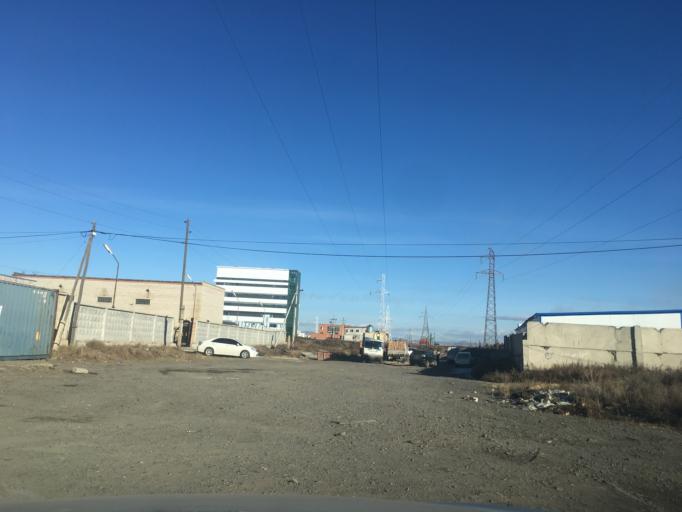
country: MN
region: Ulaanbaatar
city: Ulaanbaatar
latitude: 47.9011
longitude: 106.7907
